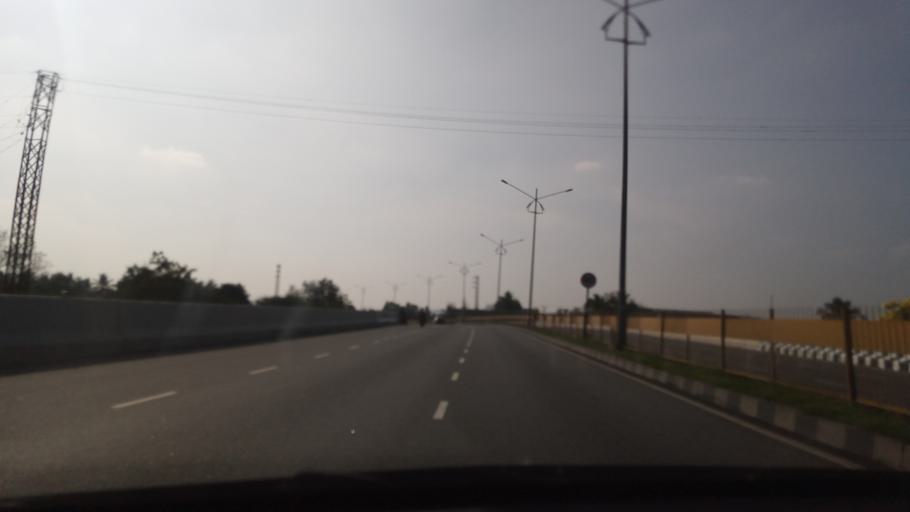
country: IN
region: Tamil Nadu
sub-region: Vellore
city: Jolarpettai
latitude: 12.5486
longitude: 78.4390
